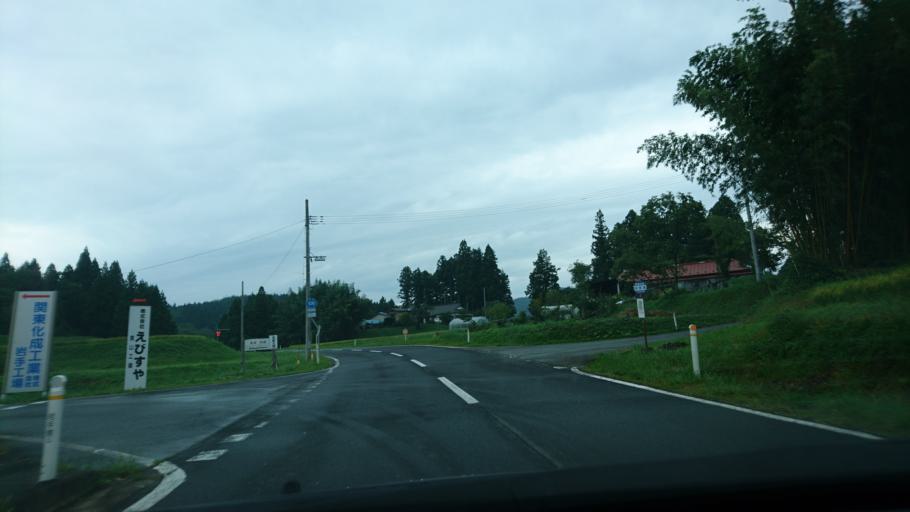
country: JP
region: Iwate
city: Ichinoseki
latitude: 39.0171
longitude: 141.2225
